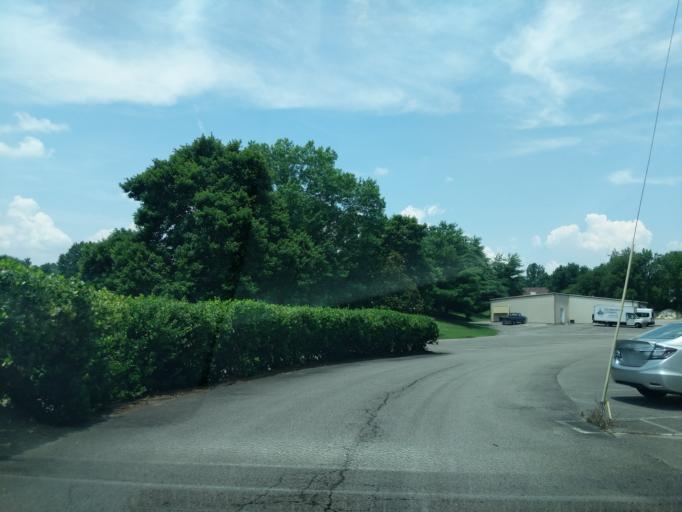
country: US
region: Tennessee
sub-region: Davidson County
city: Lakewood
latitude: 36.2355
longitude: -86.6388
